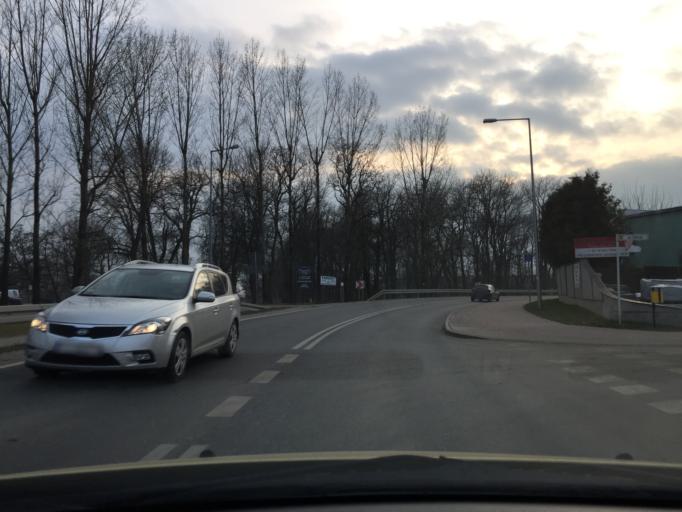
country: PL
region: Greater Poland Voivodeship
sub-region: Powiat poznanski
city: Plewiska
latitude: 52.3880
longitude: 16.7863
